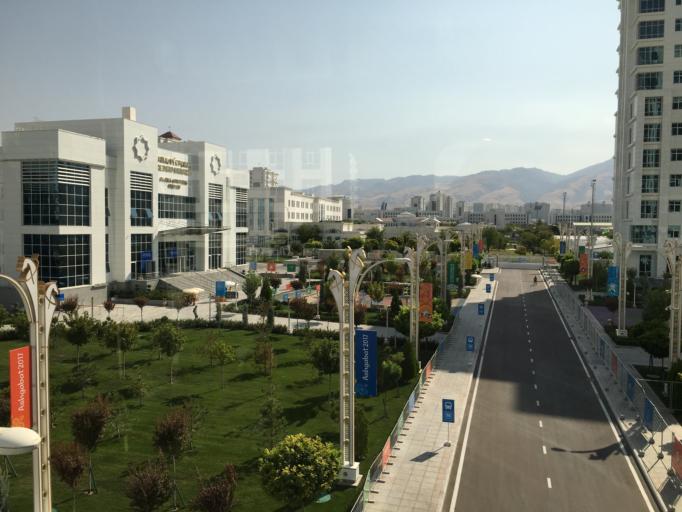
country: TM
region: Ahal
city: Ashgabat
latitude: 37.9060
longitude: 58.3706
